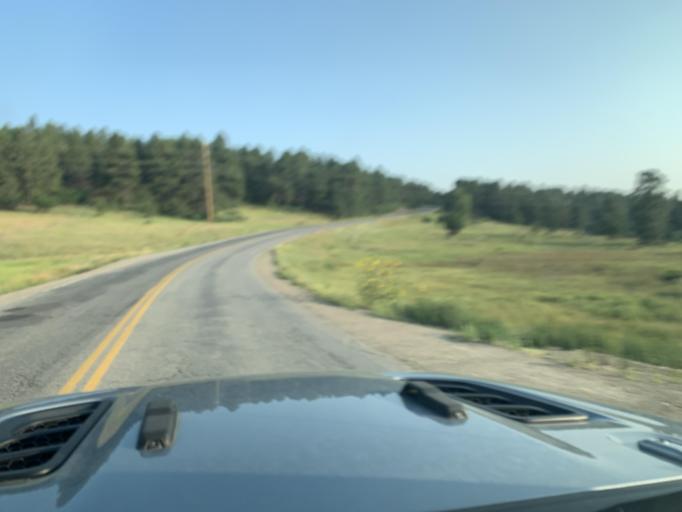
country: US
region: Colorado
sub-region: Archuleta County
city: Pagosa Springs
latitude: 37.2844
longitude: -107.0954
